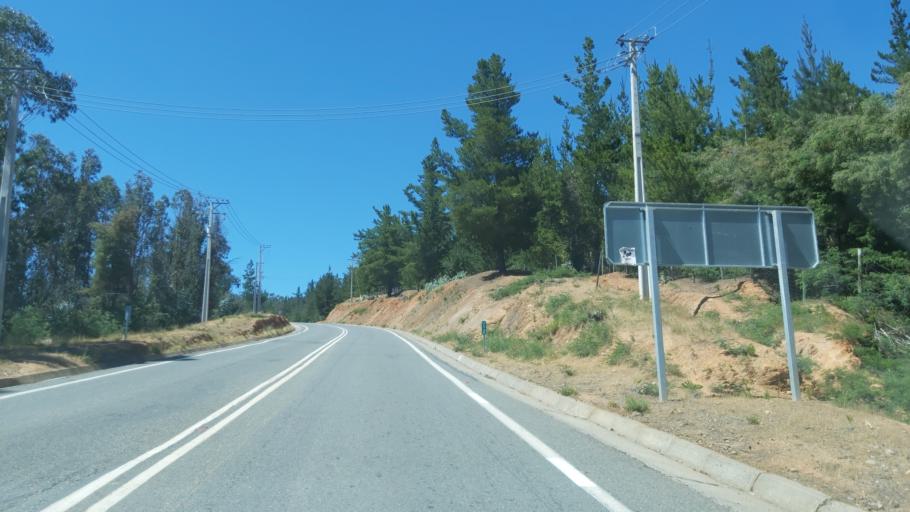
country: CL
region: Maule
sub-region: Provincia de Talca
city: Constitucion
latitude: -34.9118
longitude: -71.9962
